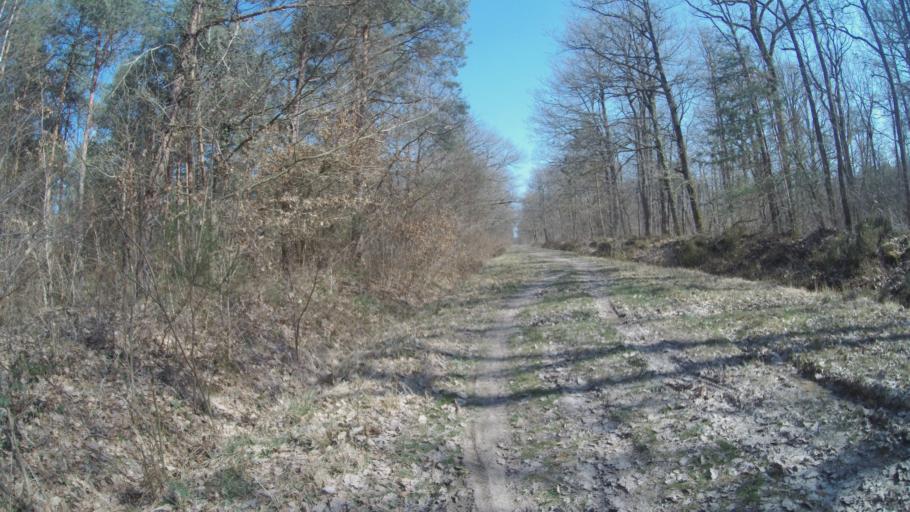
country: FR
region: Centre
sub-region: Departement du Loiret
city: Chanteau
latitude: 47.9549
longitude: 1.9633
